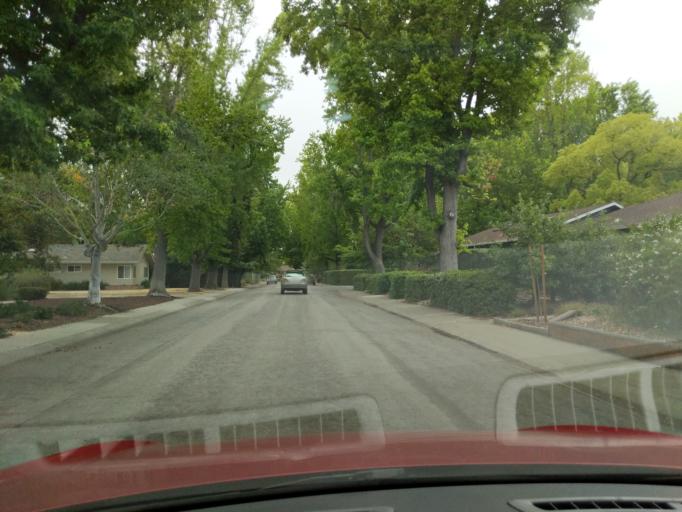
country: US
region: California
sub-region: San Mateo County
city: Menlo Park
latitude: 37.4483
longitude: -122.1701
